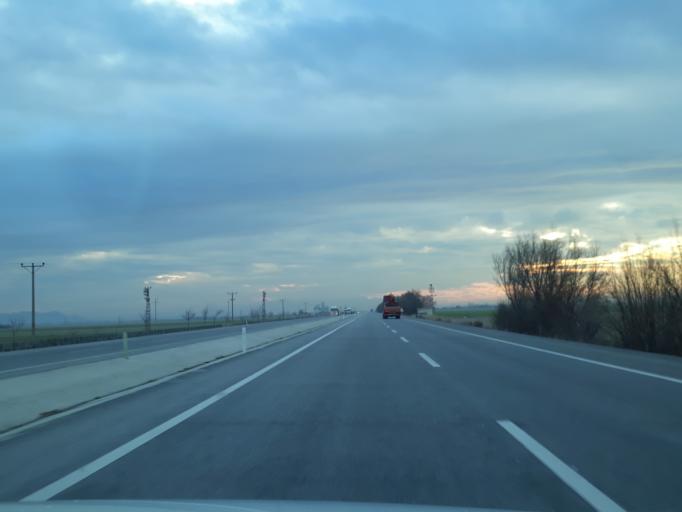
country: TR
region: Konya
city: Hotamis
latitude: 37.7117
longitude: 33.3345
